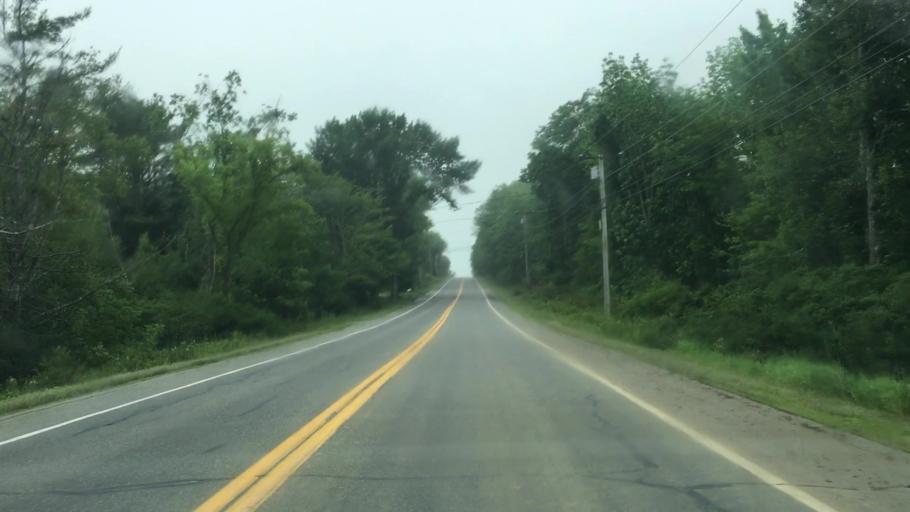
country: US
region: Maine
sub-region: Lincoln County
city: Wiscasset
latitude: 44.0631
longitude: -69.6894
